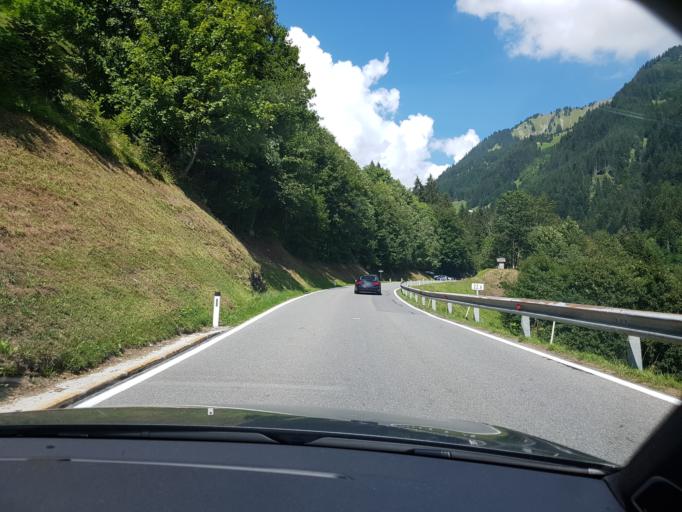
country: AT
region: Vorarlberg
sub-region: Politischer Bezirk Bregenz
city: Damuels
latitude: 47.2508
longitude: 9.9143
